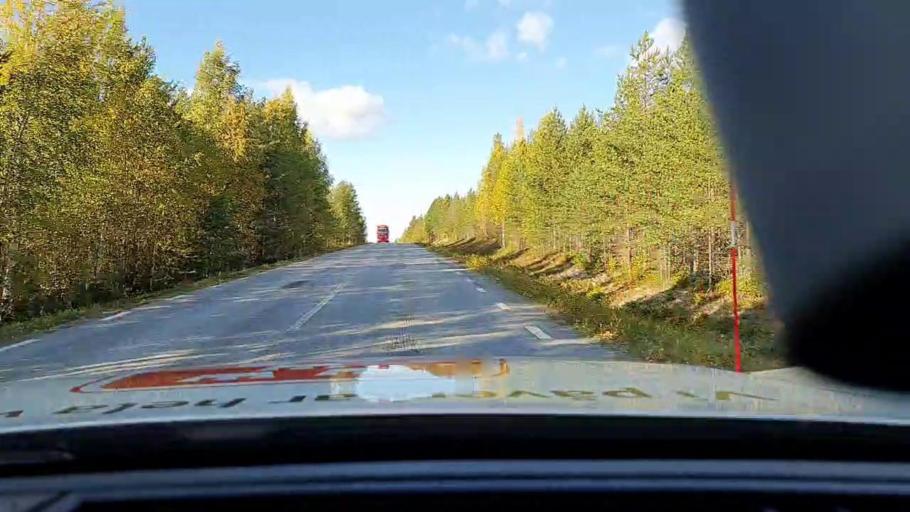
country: SE
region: Norrbotten
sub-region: Pitea Kommun
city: Norrfjarden
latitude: 65.4517
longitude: 21.4568
